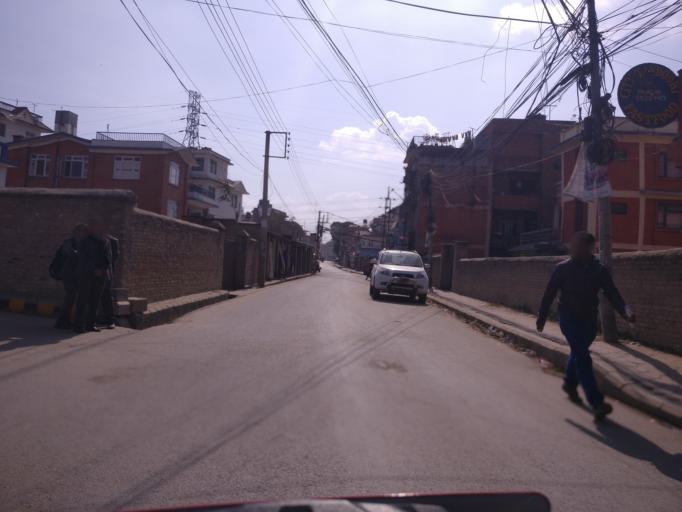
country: NP
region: Central Region
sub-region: Bagmati Zone
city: Patan
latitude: 27.6666
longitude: 85.3138
